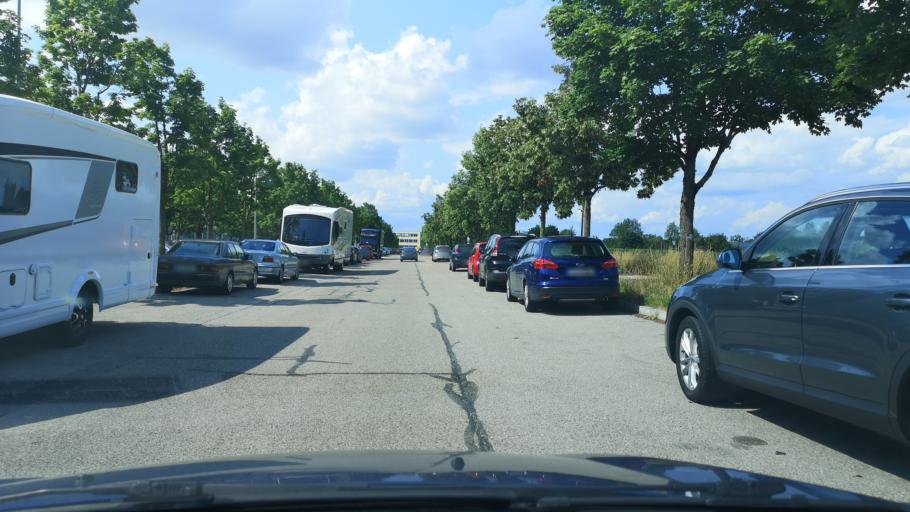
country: DE
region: Bavaria
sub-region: Upper Bavaria
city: Poing
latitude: 48.1667
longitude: 11.8028
